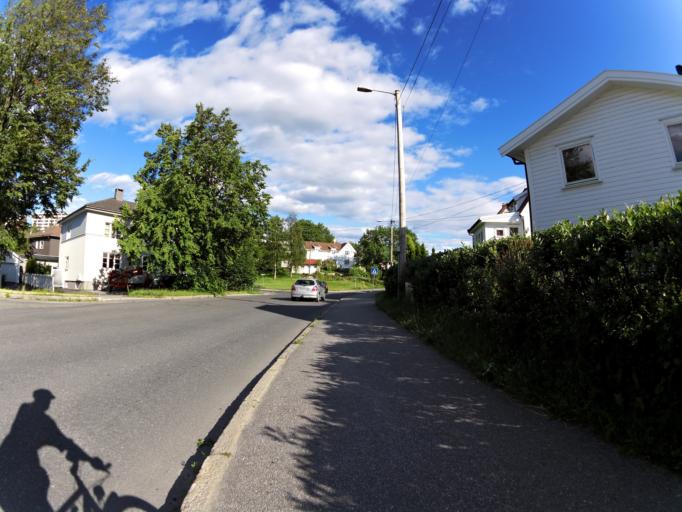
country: NO
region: Ostfold
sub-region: Fredrikstad
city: Fredrikstad
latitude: 59.2168
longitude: 10.9475
